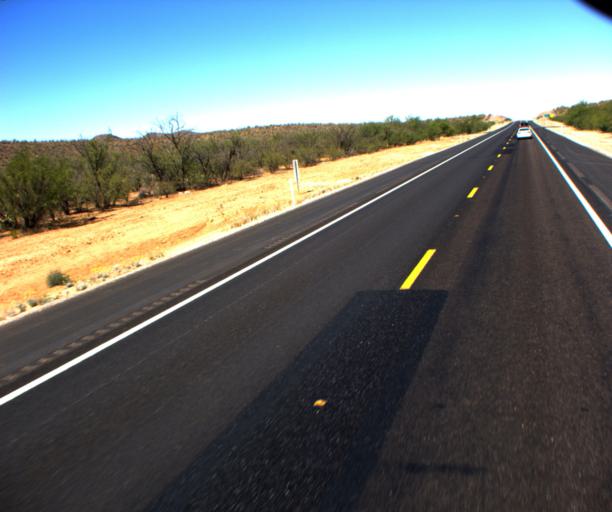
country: US
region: Arizona
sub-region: Pima County
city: Sells
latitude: 31.9172
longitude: -111.8472
